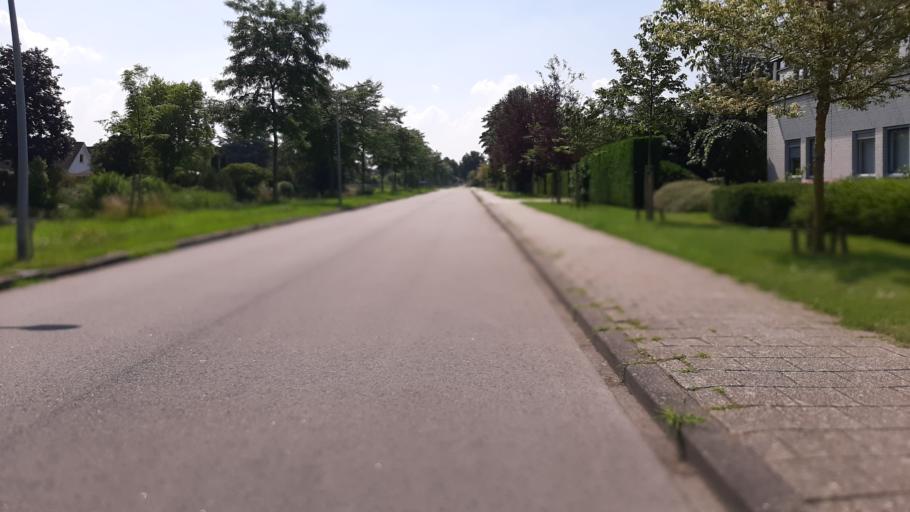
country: NL
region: Flevoland
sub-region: Gemeente Zeewolde
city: Zeewolde
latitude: 52.3263
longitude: 5.5328
